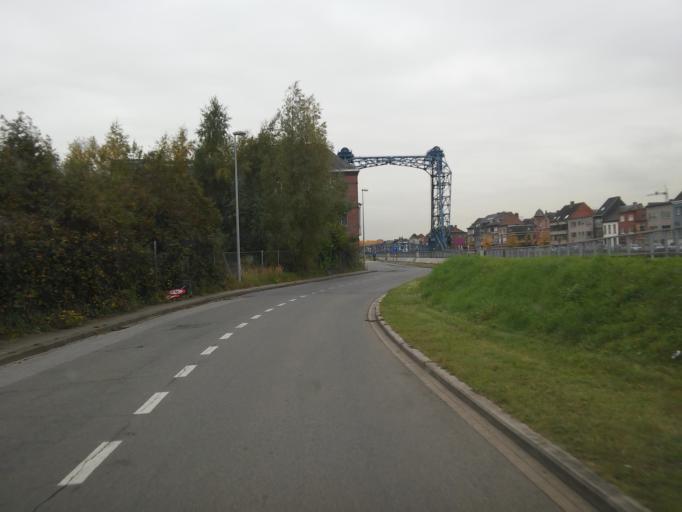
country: BE
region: Flanders
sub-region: Provincie Antwerpen
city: Willebroek
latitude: 51.0622
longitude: 4.3646
